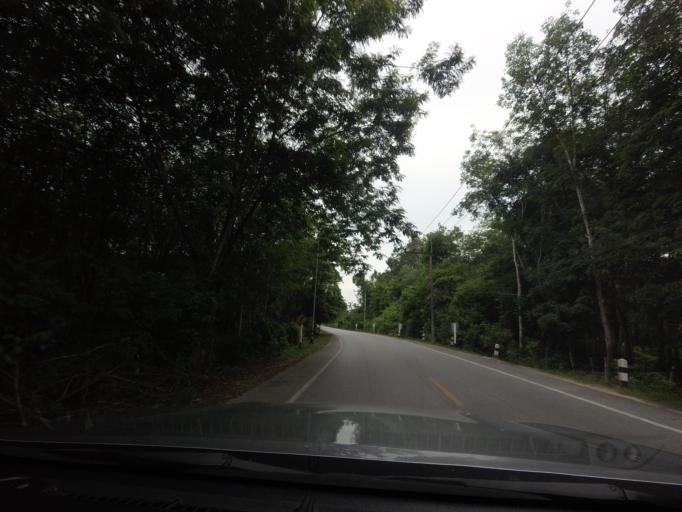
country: TH
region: Yala
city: Raman
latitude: 6.4367
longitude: 101.4547
